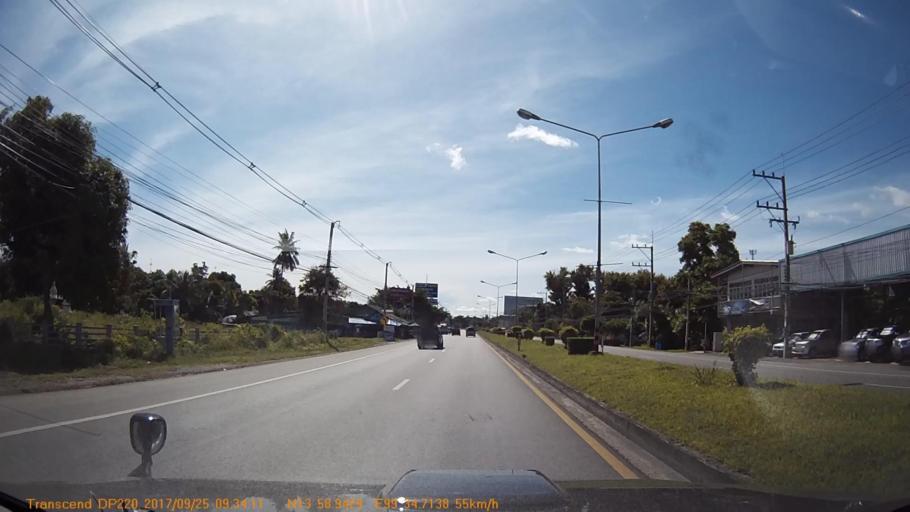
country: TH
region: Kanchanaburi
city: Kanchanaburi
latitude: 13.9823
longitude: 99.5787
